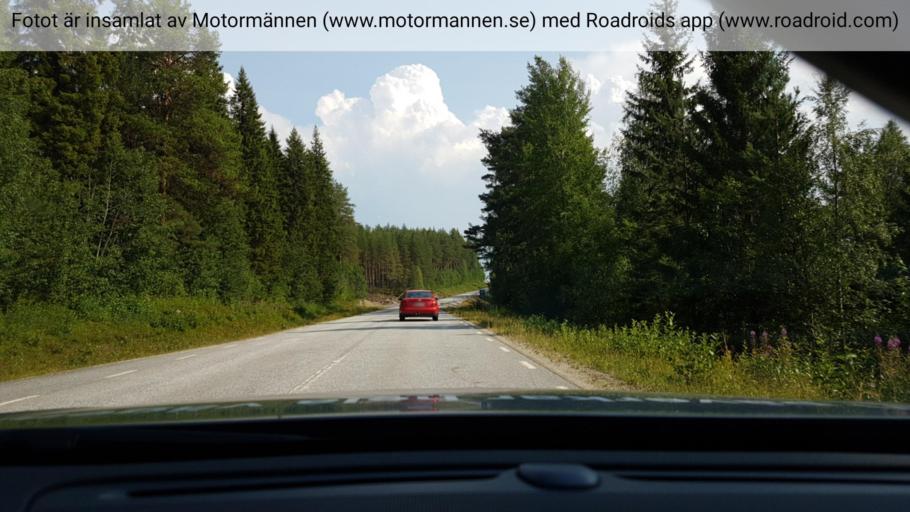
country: SE
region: Vaesterbotten
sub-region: Bjurholms Kommun
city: Bjurholm
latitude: 64.2733
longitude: 19.2607
